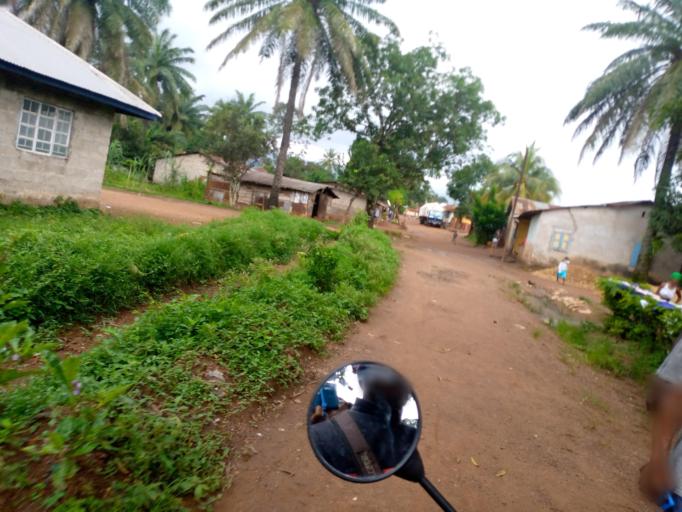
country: SL
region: Eastern Province
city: Kenema
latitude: 7.8622
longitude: -11.1888
